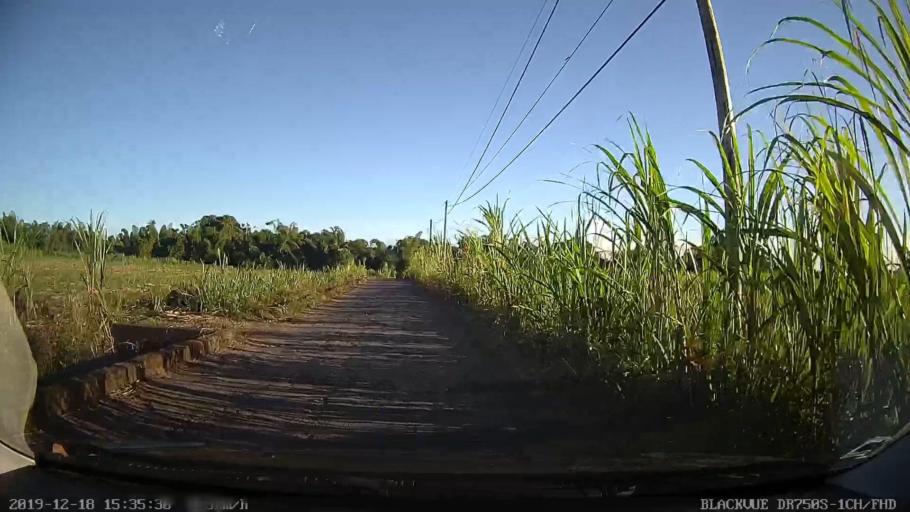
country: RE
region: Reunion
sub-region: Reunion
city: Bras-Panon
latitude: -20.9976
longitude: 55.6624
